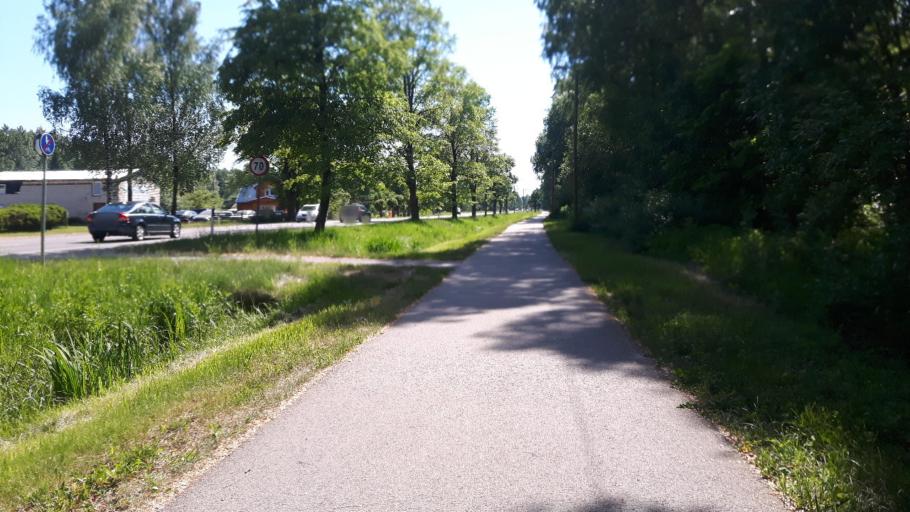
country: EE
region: Paernumaa
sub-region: Paikuse vald
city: Paikuse
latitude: 58.3822
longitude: 24.6333
